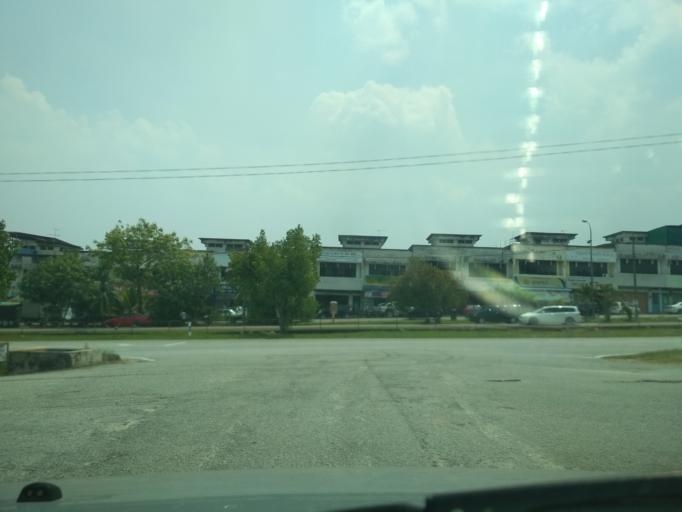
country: MY
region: Kedah
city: Kulim
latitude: 5.3542
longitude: 100.5313
